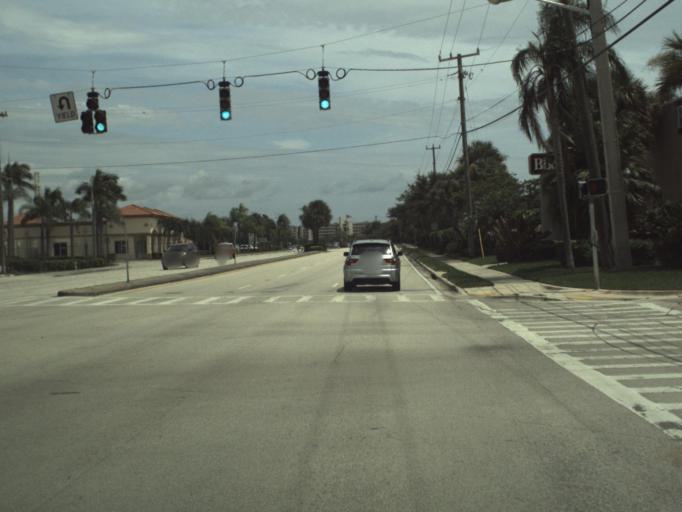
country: US
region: Florida
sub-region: Palm Beach County
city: Jupiter
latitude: 26.9592
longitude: -80.0846
